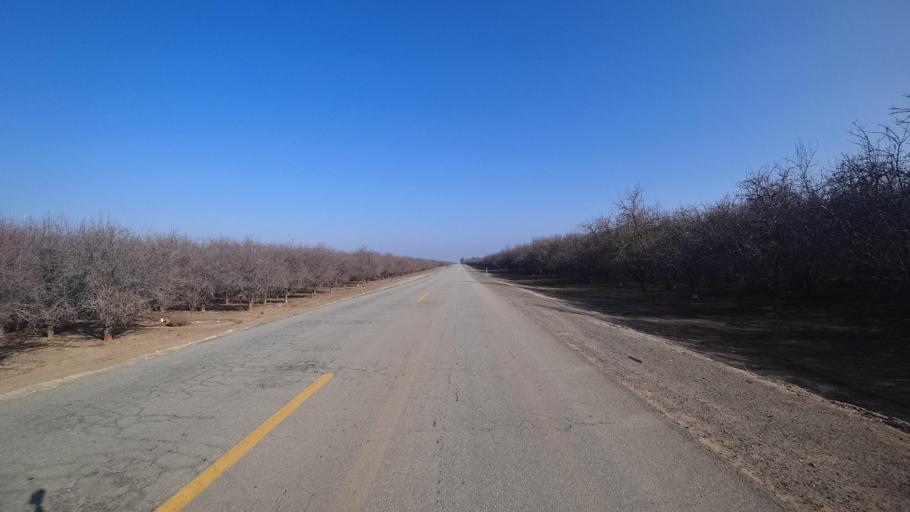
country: US
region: California
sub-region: Kern County
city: Maricopa
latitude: 35.1013
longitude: -119.3314
